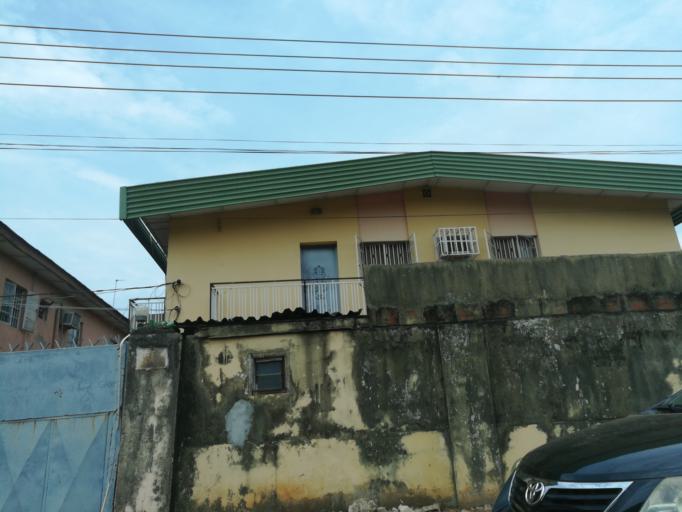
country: NG
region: Lagos
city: Oshodi
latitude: 6.5529
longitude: 3.3256
